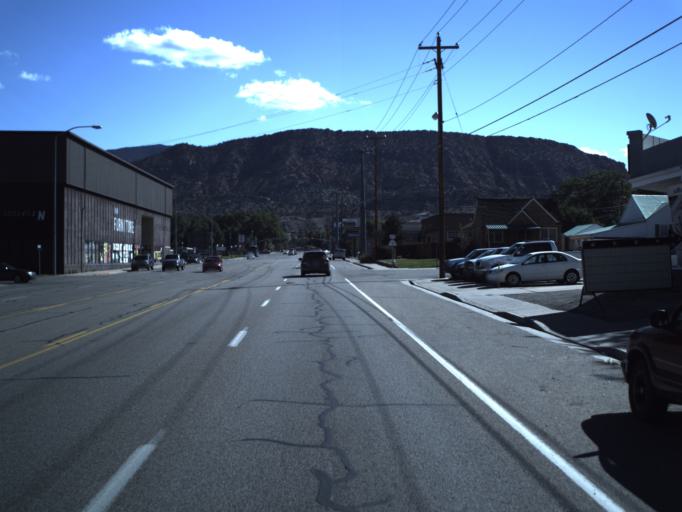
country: US
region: Utah
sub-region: Iron County
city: Cedar City
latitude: 37.6808
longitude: -113.0660
